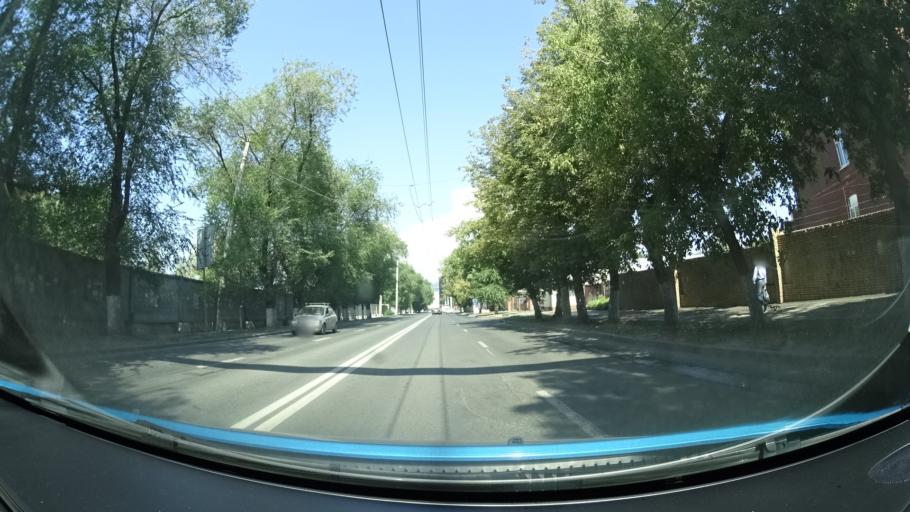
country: RU
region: Samara
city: Samara
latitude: 53.2137
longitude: 50.1525
